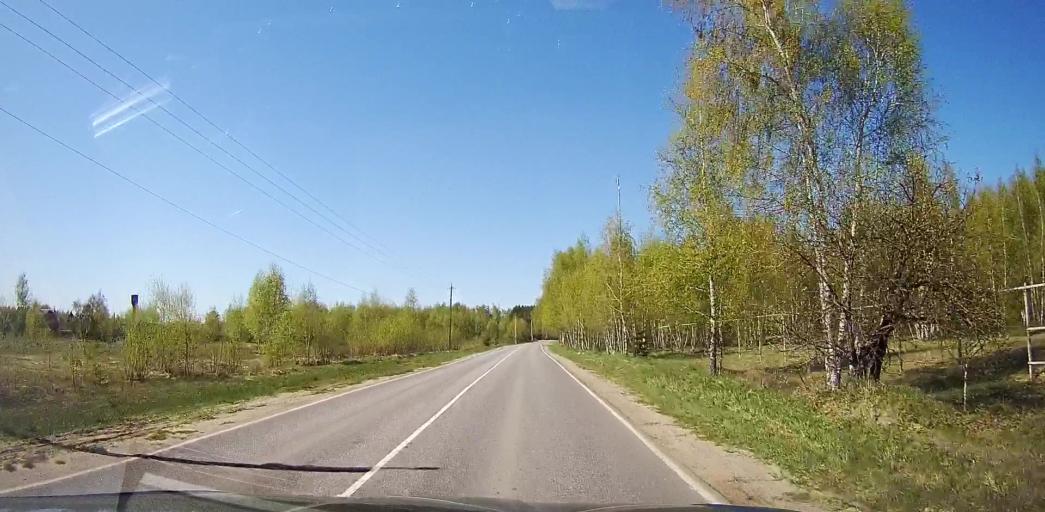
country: RU
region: Moskovskaya
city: Bronnitsy
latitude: 55.4665
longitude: 38.2806
